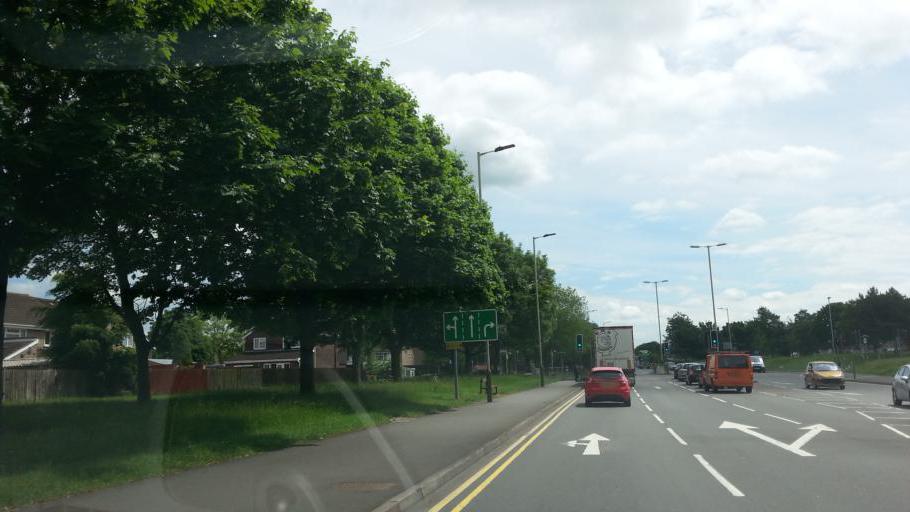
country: GB
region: England
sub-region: Leicestershire
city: Syston
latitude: 52.6659
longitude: -1.1019
